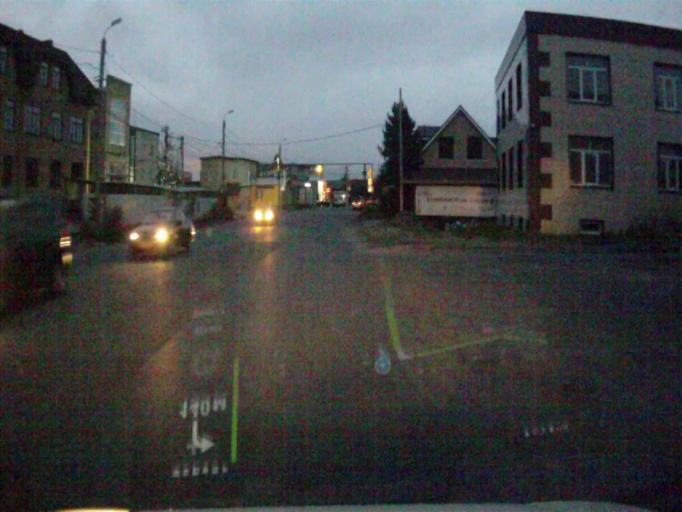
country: RU
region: Chelyabinsk
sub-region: Gorod Chelyabinsk
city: Chelyabinsk
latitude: 55.1557
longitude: 61.3011
